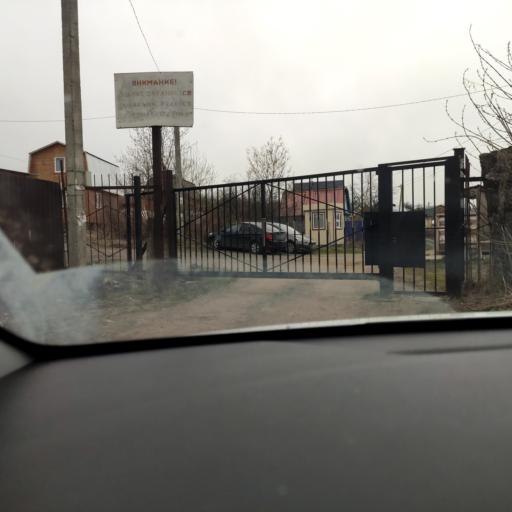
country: RU
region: Tatarstan
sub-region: Gorod Kazan'
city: Kazan
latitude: 55.8928
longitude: 49.0793
